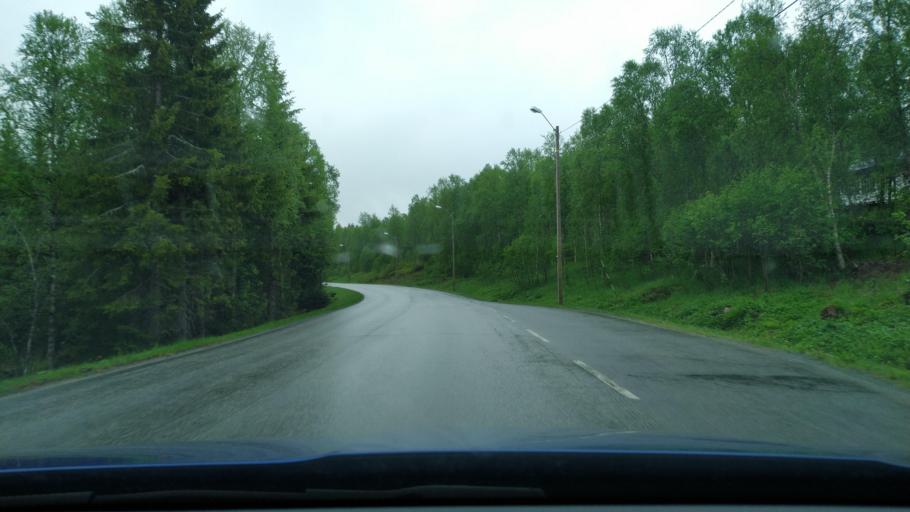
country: NO
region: Troms
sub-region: Dyroy
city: Brostadbotn
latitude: 69.0469
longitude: 17.7313
